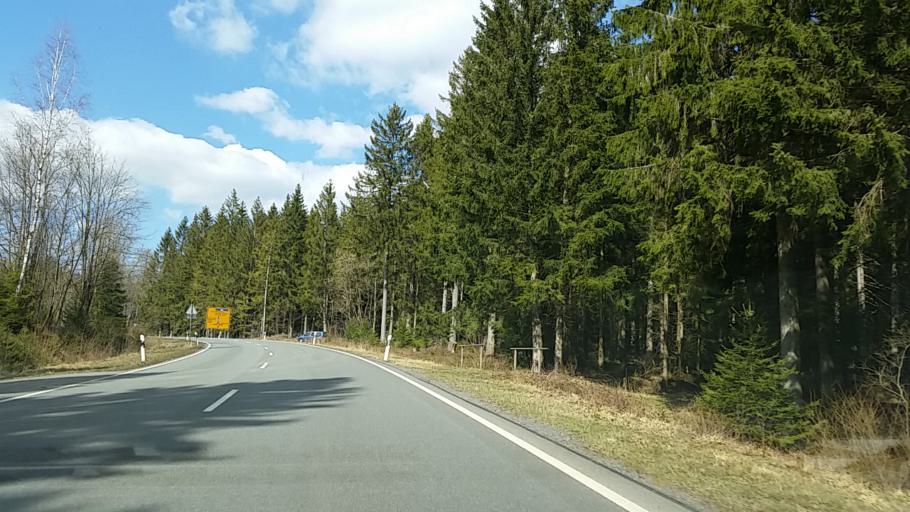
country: DE
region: Lower Saxony
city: Braunlage
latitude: 51.7120
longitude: 10.6292
